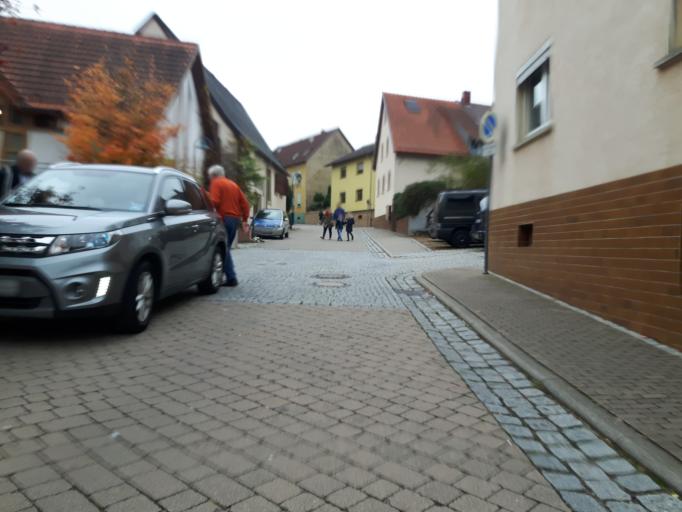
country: DE
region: Baden-Wuerttemberg
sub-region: Karlsruhe Region
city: Ostringen
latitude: 49.2175
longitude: 8.7091
